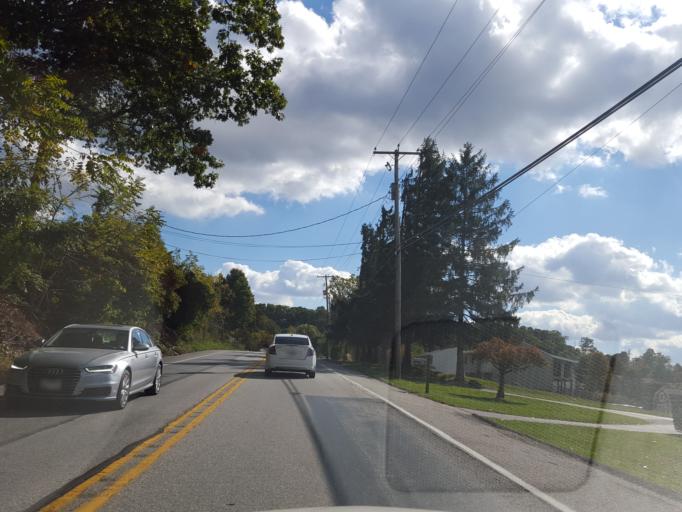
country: US
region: Pennsylvania
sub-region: York County
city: Yoe
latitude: 39.9348
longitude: -76.6439
